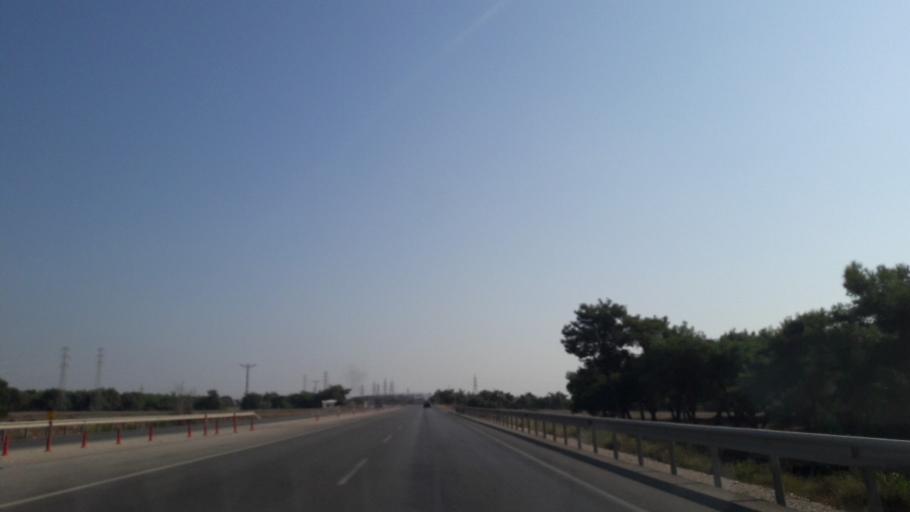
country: TR
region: Adana
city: Yakapinar
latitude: 37.0940
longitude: 35.4992
